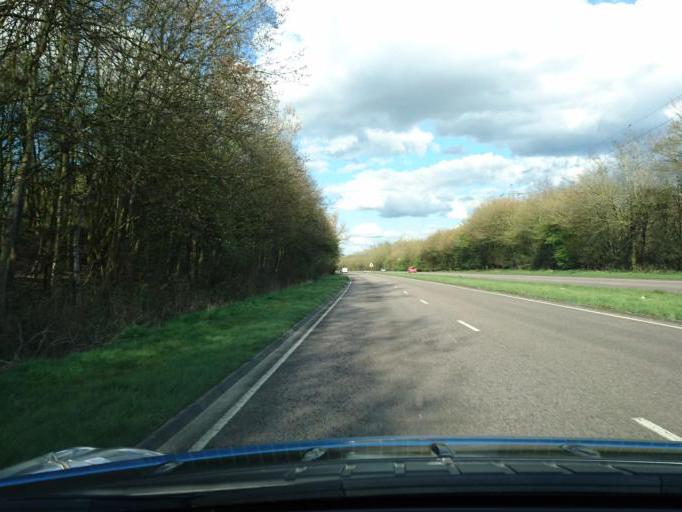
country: GB
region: England
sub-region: Wiltshire
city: Lydiard Tregoze
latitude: 51.5492
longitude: -1.8217
